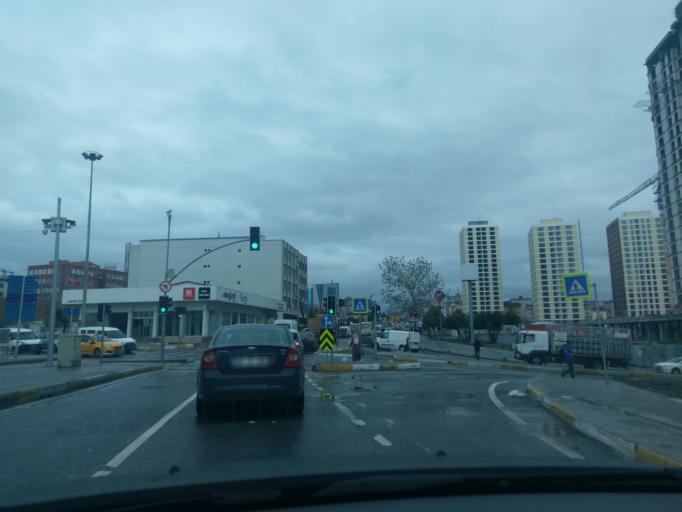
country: TR
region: Istanbul
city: Mahmutbey
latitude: 41.0527
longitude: 28.8301
